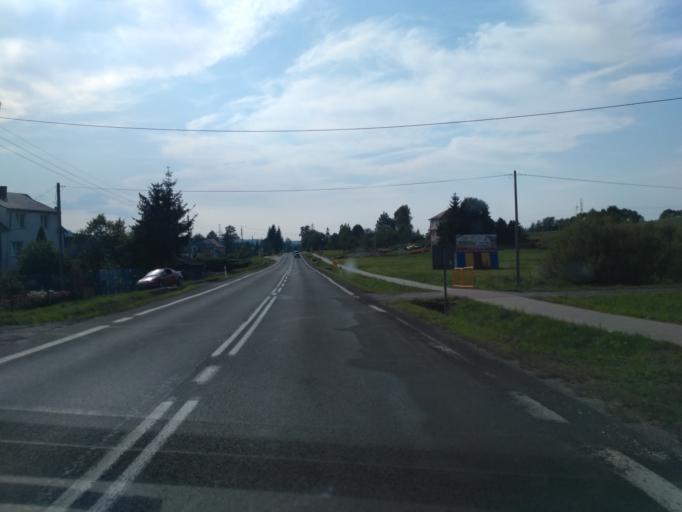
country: PL
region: Subcarpathian Voivodeship
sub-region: Powiat bieszczadzki
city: Ustrzyki Dolne
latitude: 49.4282
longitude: 22.5402
